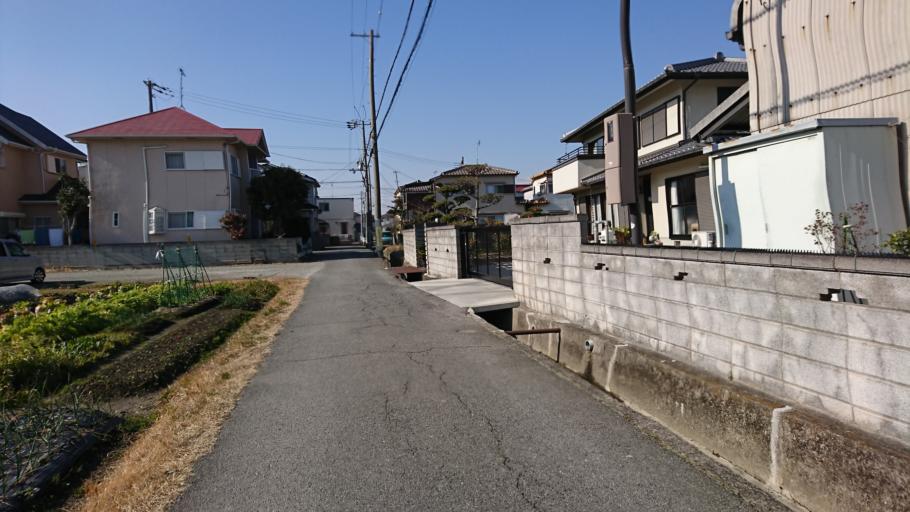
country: JP
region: Hyogo
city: Kakogawacho-honmachi
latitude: 34.7414
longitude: 134.8551
